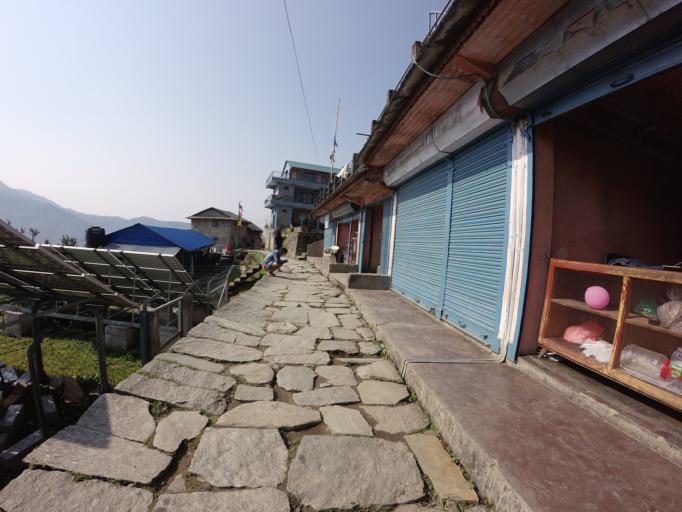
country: NP
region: Western Region
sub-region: Dhawalagiri Zone
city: Chitre
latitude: 28.3769
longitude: 83.8088
